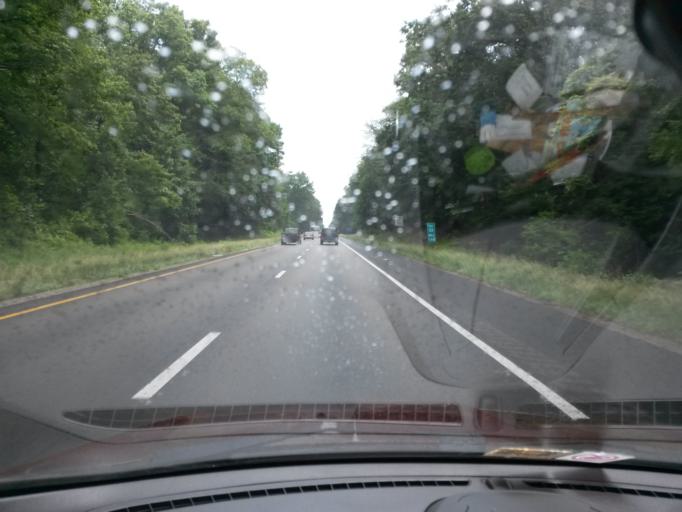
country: US
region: Virginia
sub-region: Goochland County
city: Goochland
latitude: 37.7072
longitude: -77.7720
